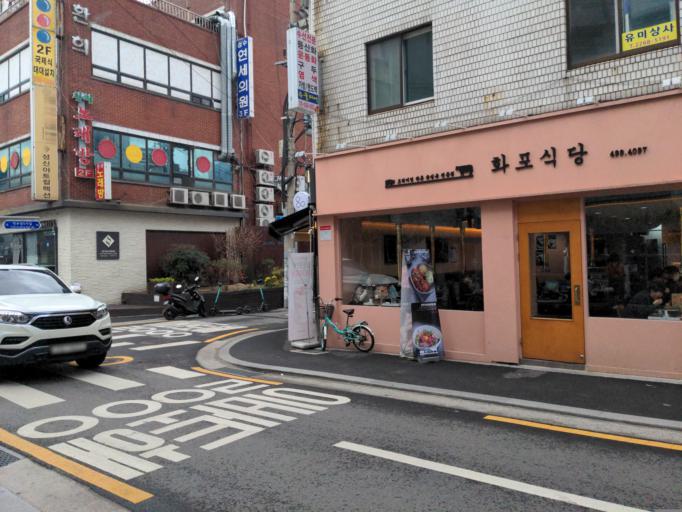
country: KR
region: Seoul
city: Seoul
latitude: 37.5435
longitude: 127.0546
